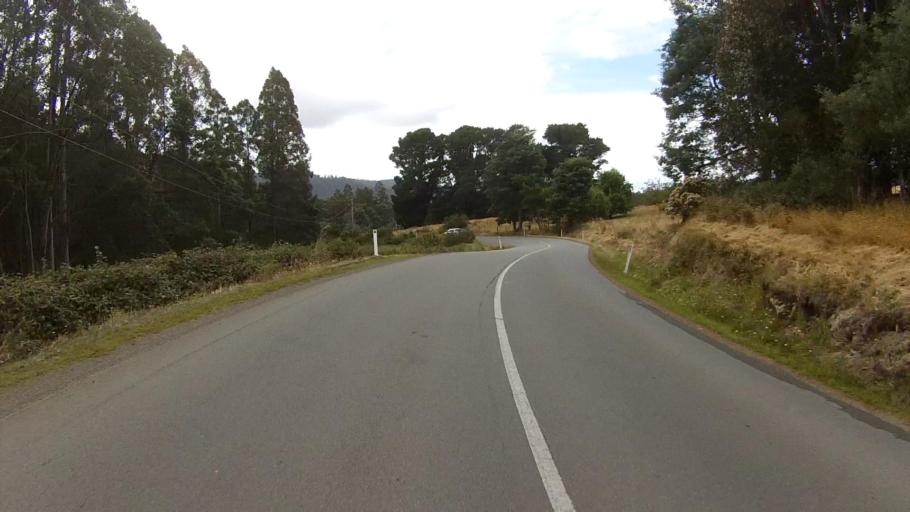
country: AU
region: Tasmania
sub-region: Kingborough
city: Kettering
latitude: -43.1133
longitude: 147.1935
